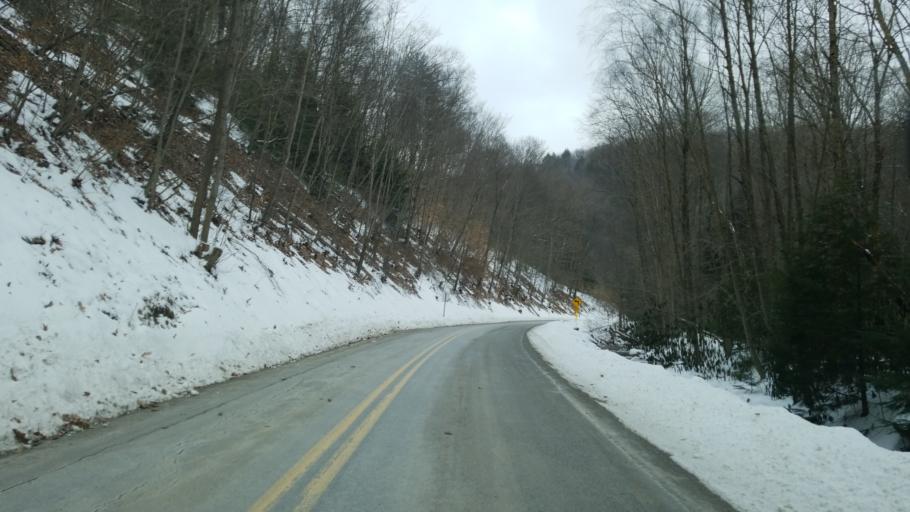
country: US
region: Pennsylvania
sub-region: Clearfield County
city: Shiloh
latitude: 41.2473
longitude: -78.1576
